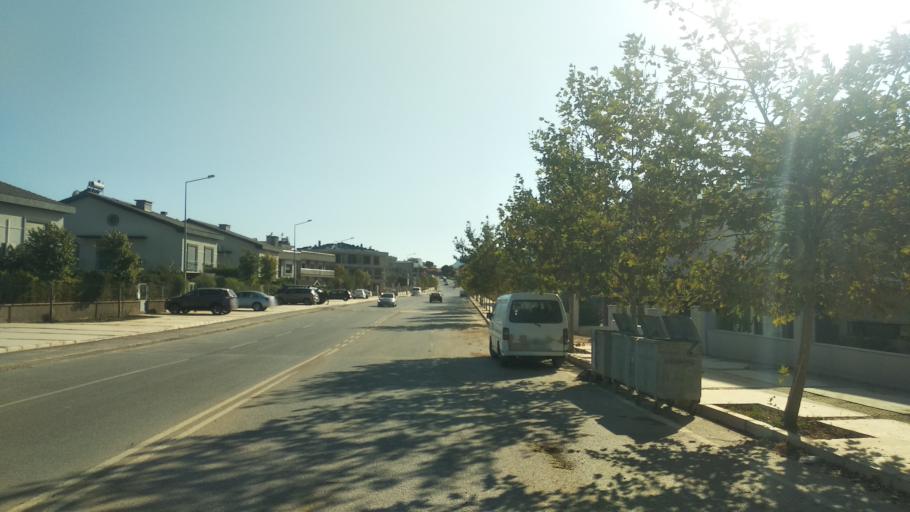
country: TR
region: Izmir
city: Urla
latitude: 38.3572
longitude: 26.8734
